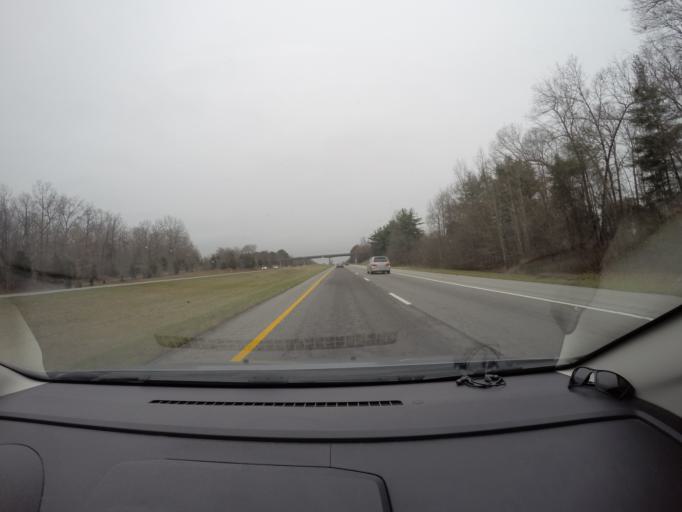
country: US
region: Tennessee
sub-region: Coffee County
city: Manchester
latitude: 35.3993
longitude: -85.9981
